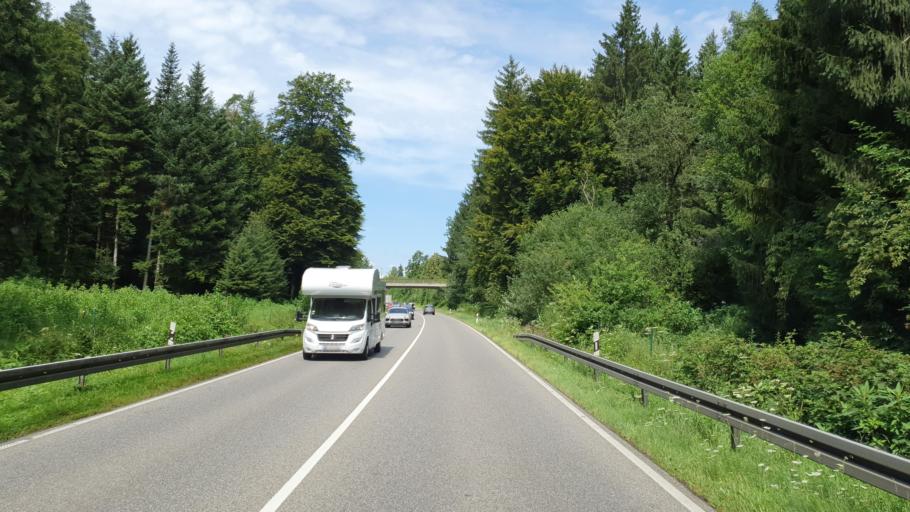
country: DE
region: Bavaria
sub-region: Swabia
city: Nonnenhorn
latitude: 47.5931
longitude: 9.6413
